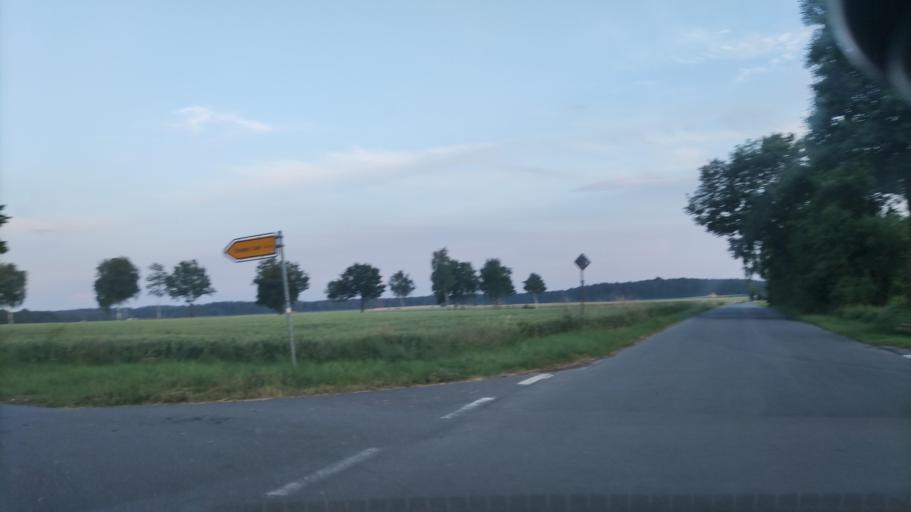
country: DE
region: Lower Saxony
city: Egestorf
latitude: 53.1405
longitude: 10.0313
